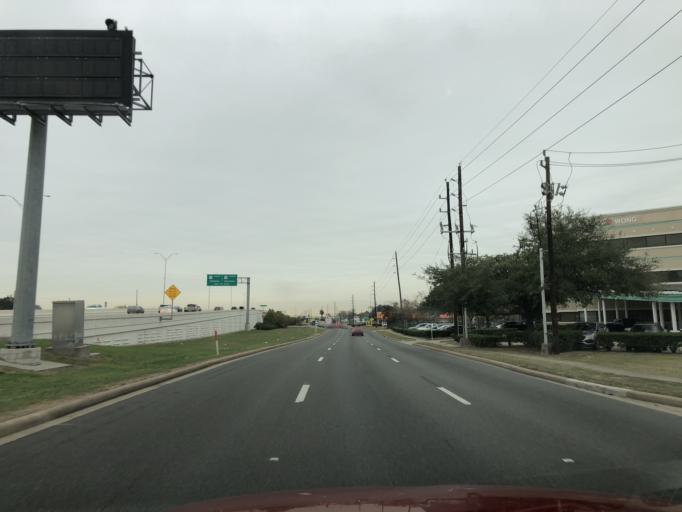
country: US
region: Texas
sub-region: Fort Bend County
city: Missouri City
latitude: 29.6424
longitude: -95.5365
